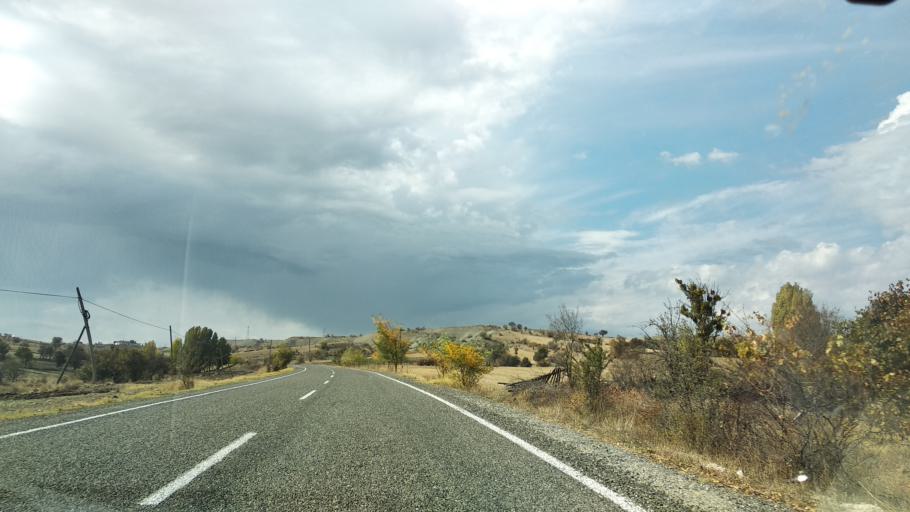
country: TR
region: Bolu
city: Seben
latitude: 40.3828
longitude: 31.5279
